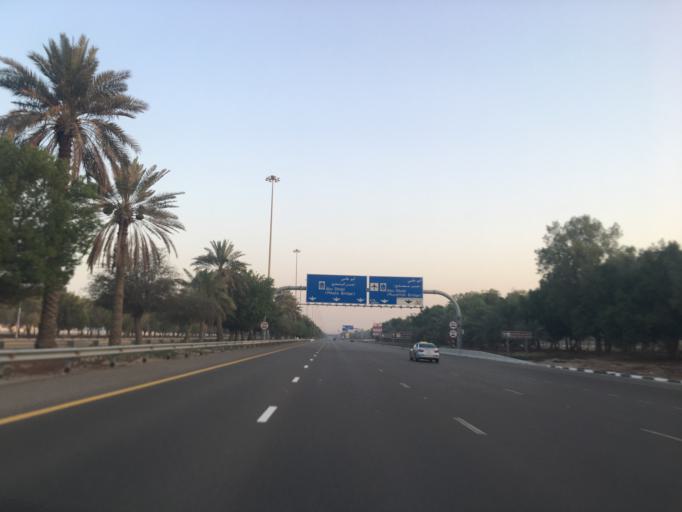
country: AE
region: Abu Dhabi
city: Abu Dhabi
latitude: 24.3803
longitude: 54.5478
